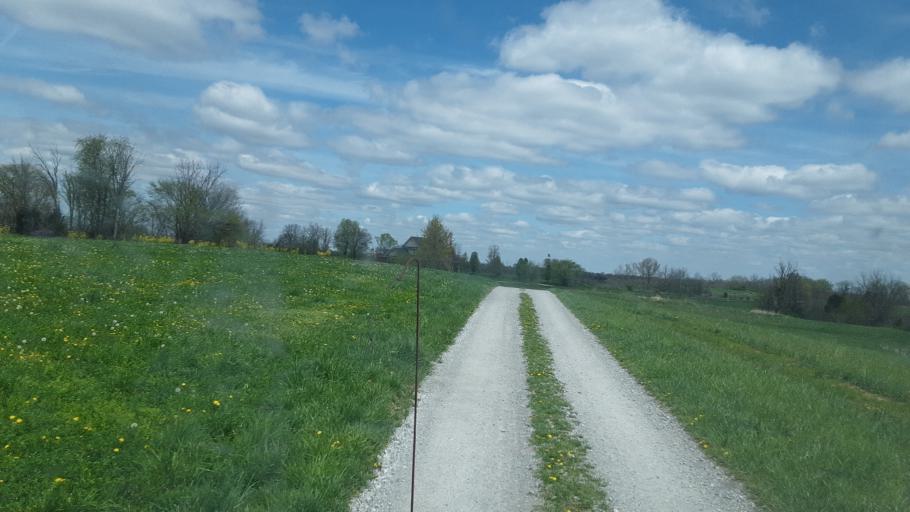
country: US
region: Kentucky
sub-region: Gallatin County
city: Warsaw
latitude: 38.6769
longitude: -84.8123
